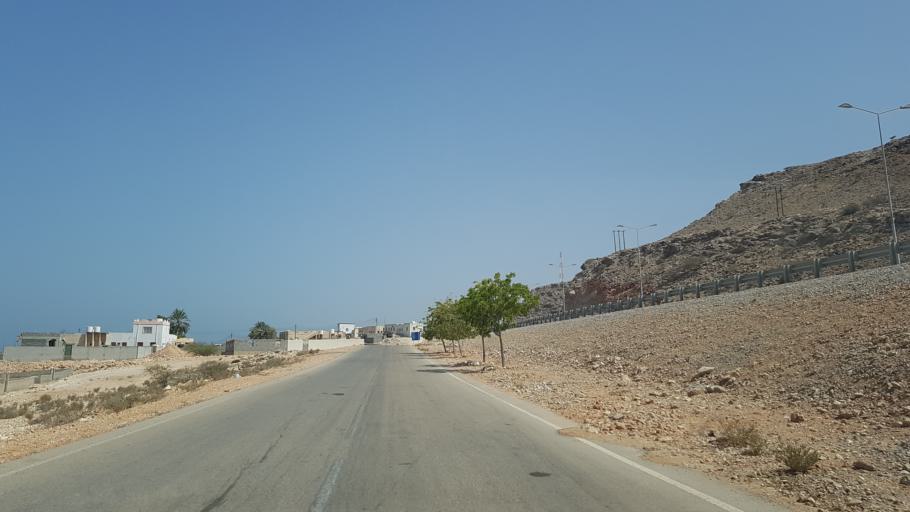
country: OM
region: Ash Sharqiyah
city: Sur
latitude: 22.8423
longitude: 59.2436
